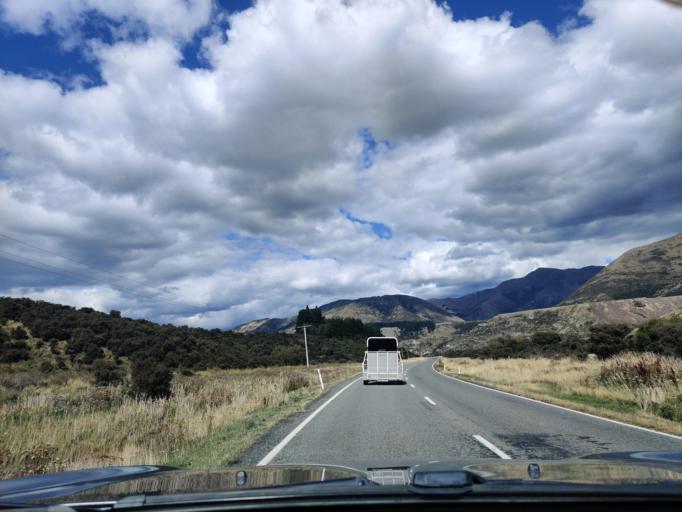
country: NZ
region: Canterbury
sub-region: Hurunui District
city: Amberley
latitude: -42.5894
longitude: 172.3999
